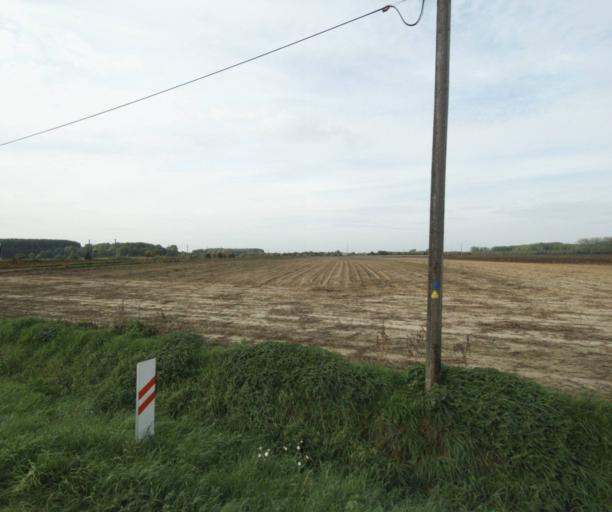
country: FR
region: Nord-Pas-de-Calais
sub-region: Departement du Nord
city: Don
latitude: 50.5485
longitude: 2.9045
